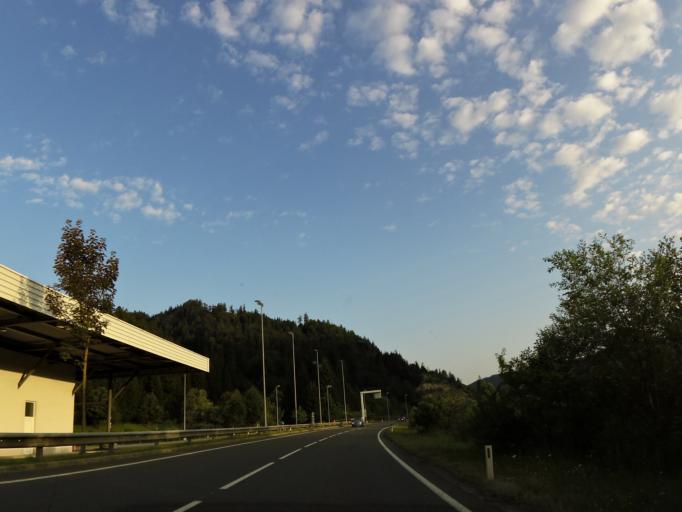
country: AT
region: Tyrol
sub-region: Politischer Bezirk Reutte
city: Musau
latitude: 47.5396
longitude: 10.6679
